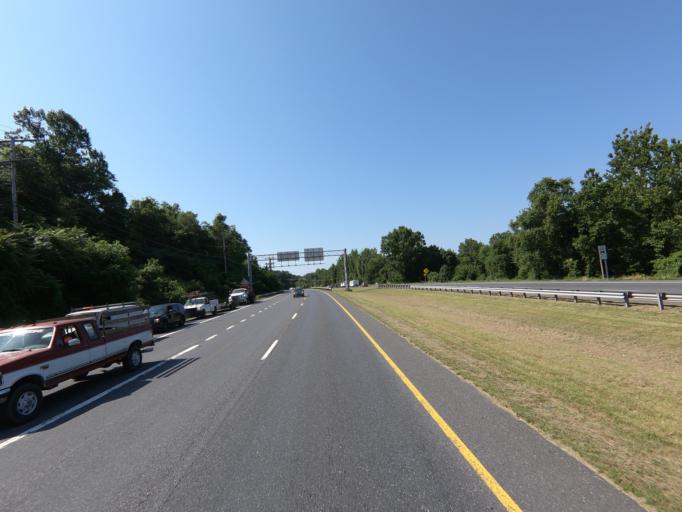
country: US
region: Maryland
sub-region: Carroll County
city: Sykesville
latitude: 39.3048
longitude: -76.9529
